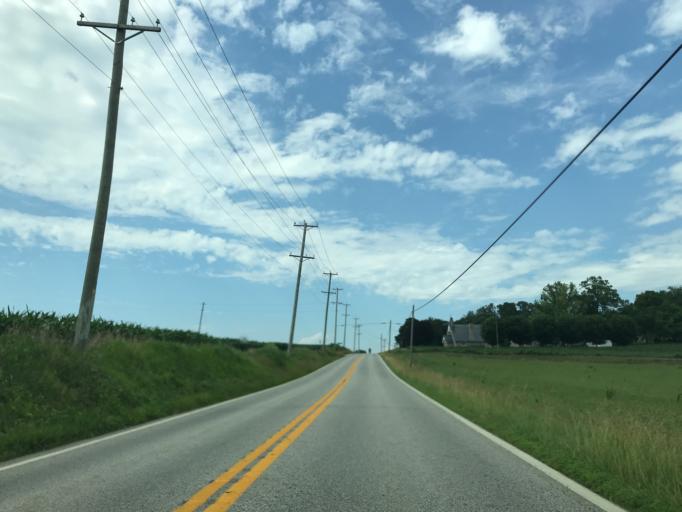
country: US
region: Maryland
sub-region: Harford County
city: Jarrettsville
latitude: 39.6630
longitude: -76.4075
